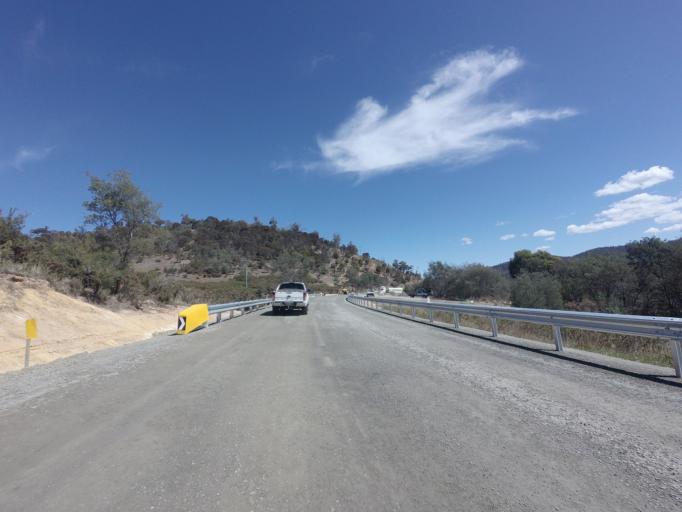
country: AU
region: Tasmania
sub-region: Break O'Day
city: St Helens
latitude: -41.6557
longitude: 147.9222
